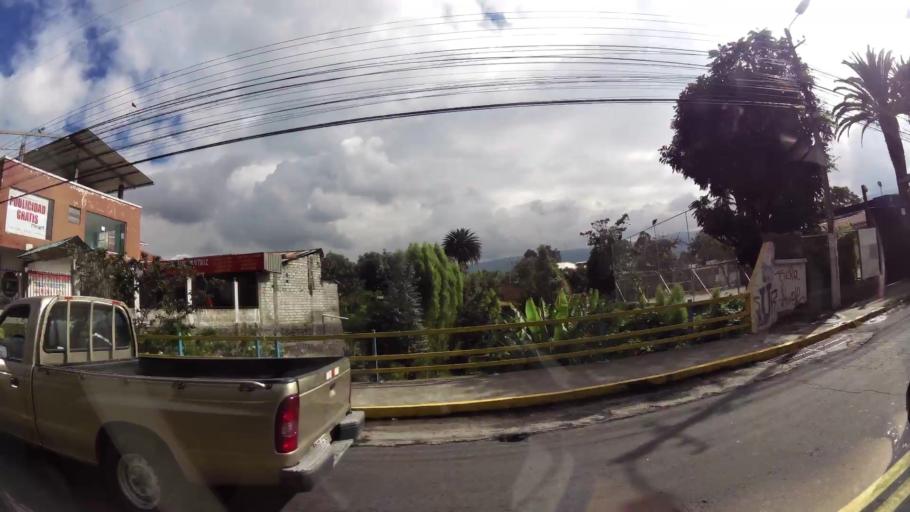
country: EC
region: Pichincha
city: Sangolqui
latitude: -0.3034
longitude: -78.4571
